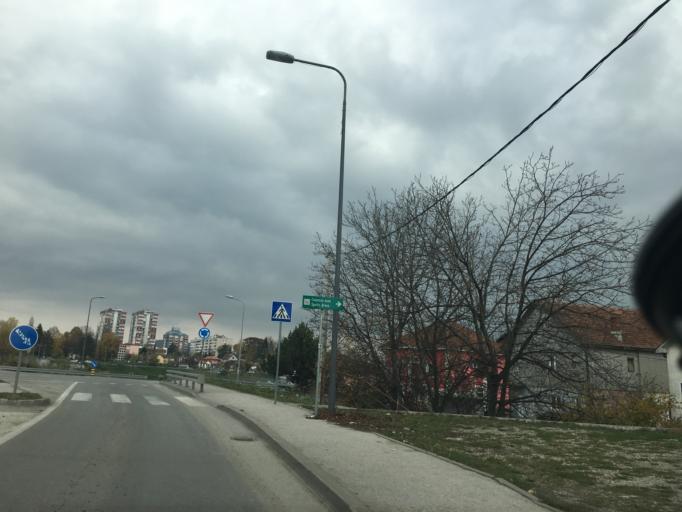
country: RS
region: Central Serbia
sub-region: Raski Okrug
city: Kraljevo
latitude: 43.7183
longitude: 20.6861
